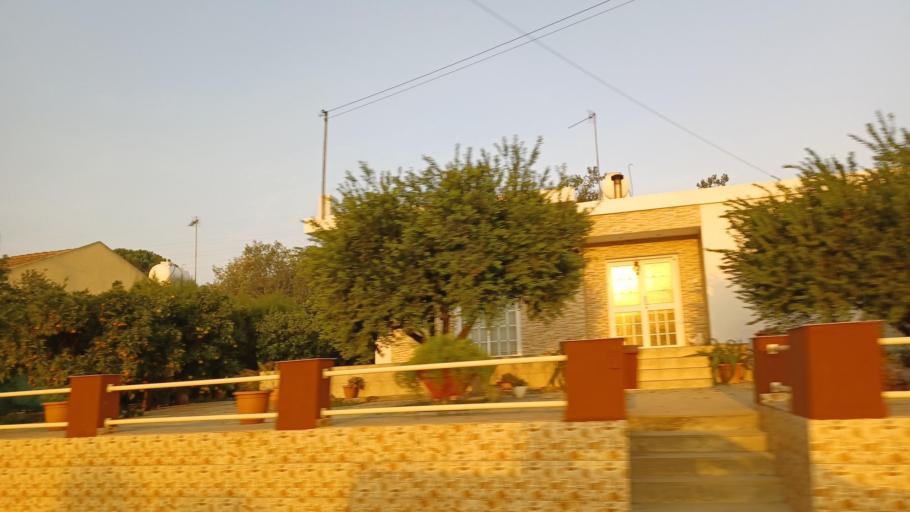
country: CY
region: Larnaka
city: Mosfiloti
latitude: 34.9523
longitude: 33.4202
